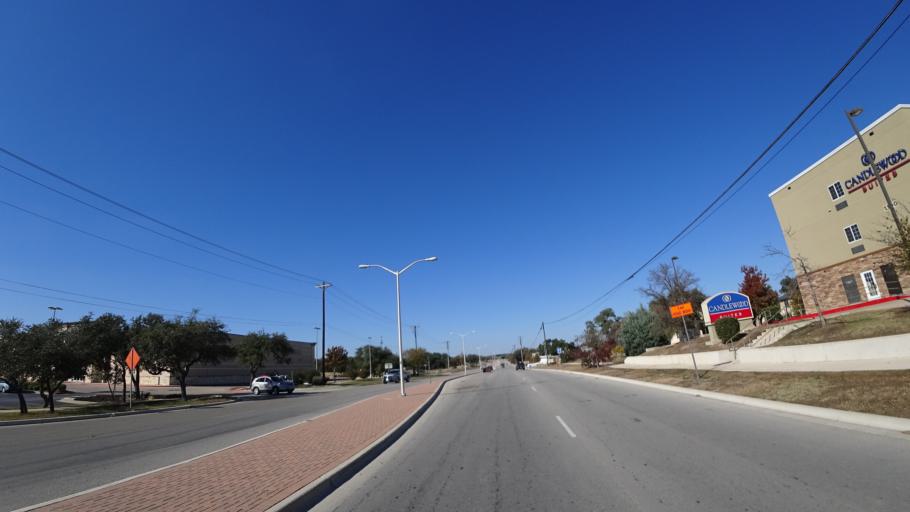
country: US
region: Texas
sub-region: Williamson County
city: Cedar Park
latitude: 30.5292
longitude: -97.8061
